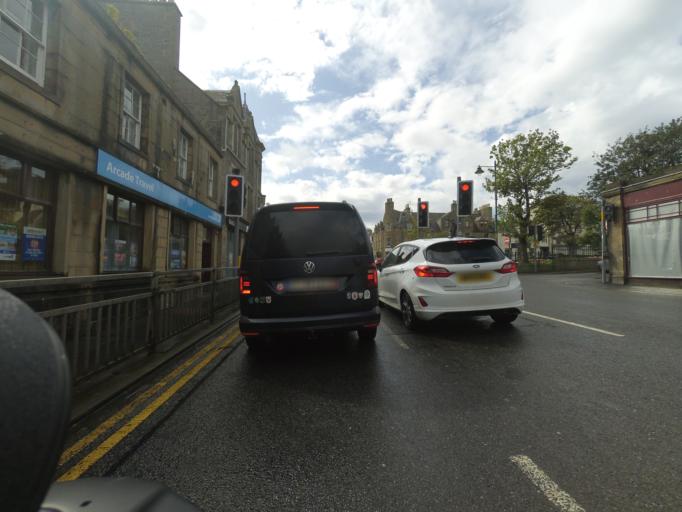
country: GB
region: Scotland
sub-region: Highland
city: Thurso
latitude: 58.5937
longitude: -3.5216
